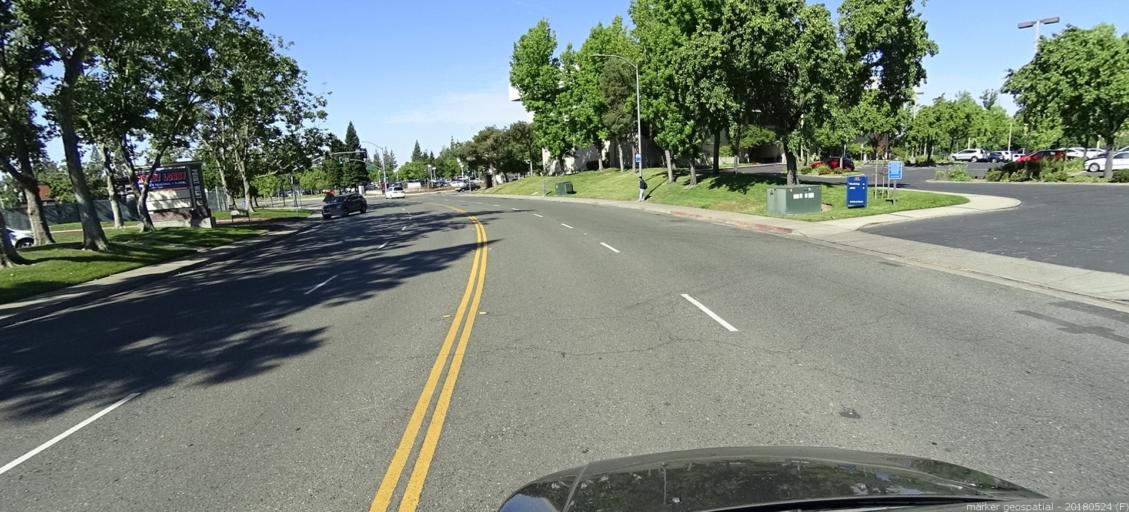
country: US
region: California
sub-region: Sacramento County
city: Arden-Arcade
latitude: 38.5969
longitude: -121.4270
